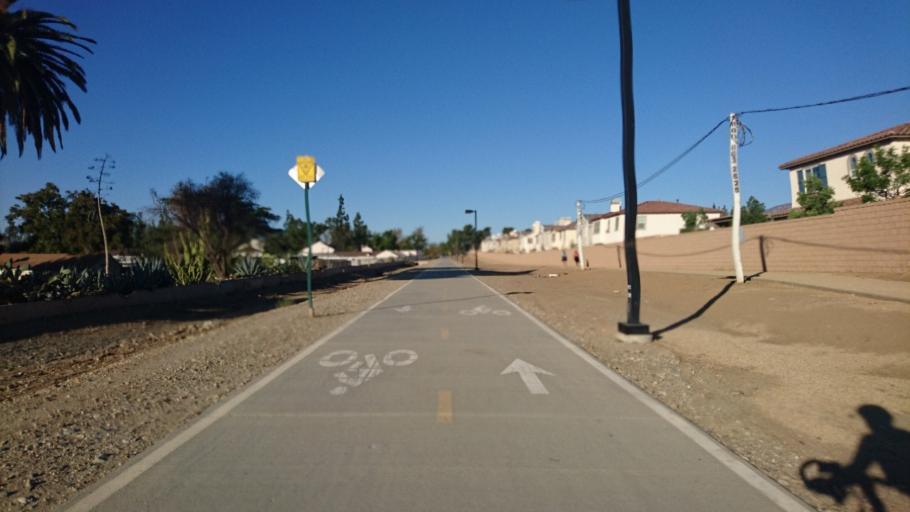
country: US
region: California
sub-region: San Bernardino County
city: Rancho Cucamonga
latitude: 34.1255
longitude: -117.5898
